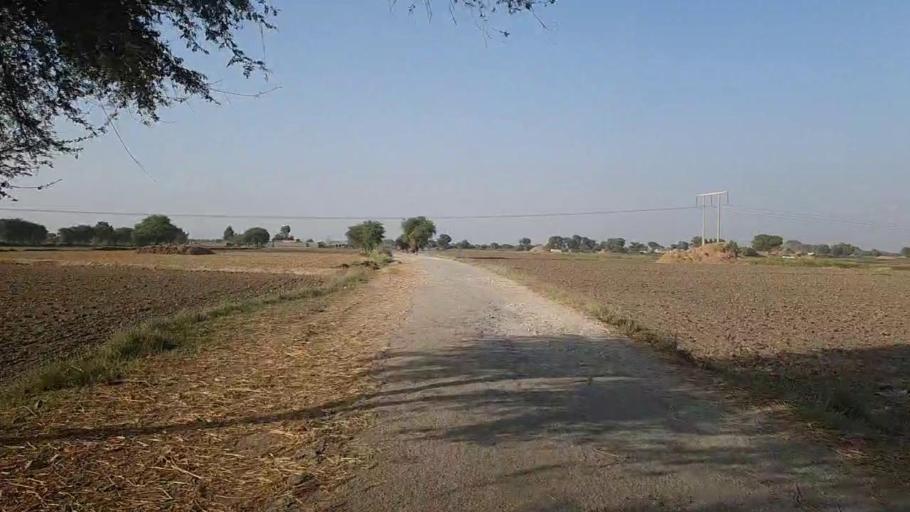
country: PK
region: Sindh
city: Kashmor
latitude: 28.4097
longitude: 69.4122
